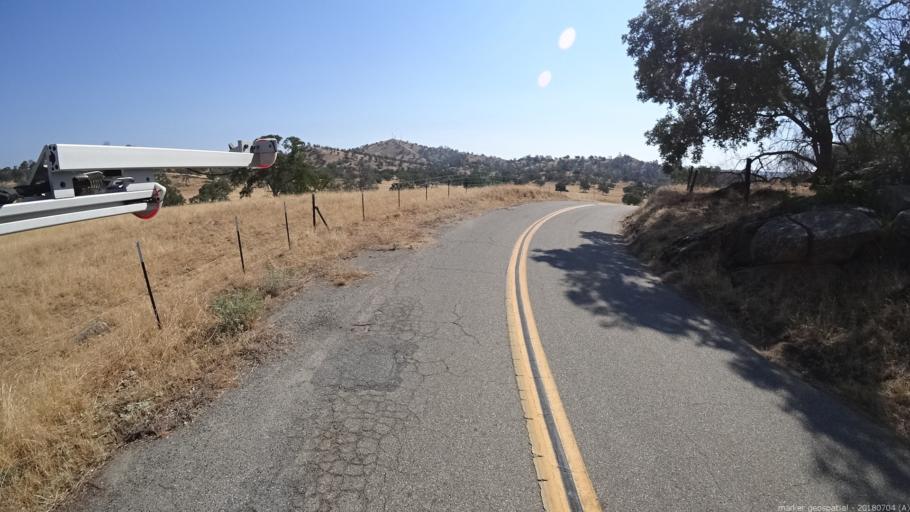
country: US
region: California
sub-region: Madera County
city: Yosemite Lakes
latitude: 37.1153
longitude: -119.6944
